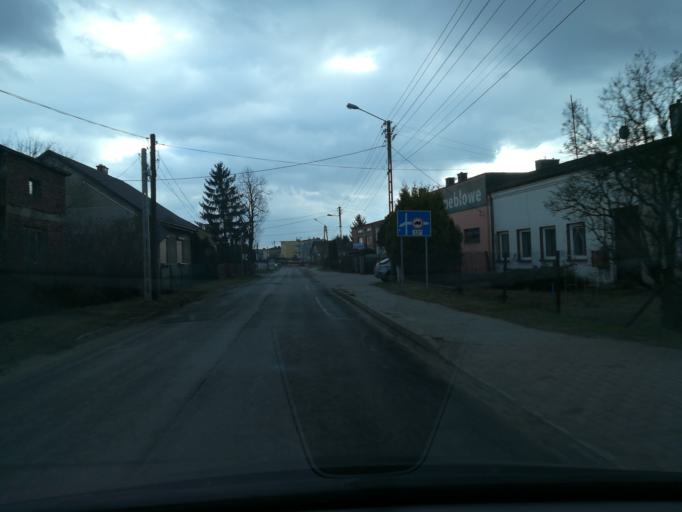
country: PL
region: Lodz Voivodeship
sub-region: Powiat radomszczanski
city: Radomsko
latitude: 51.0680
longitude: 19.4222
